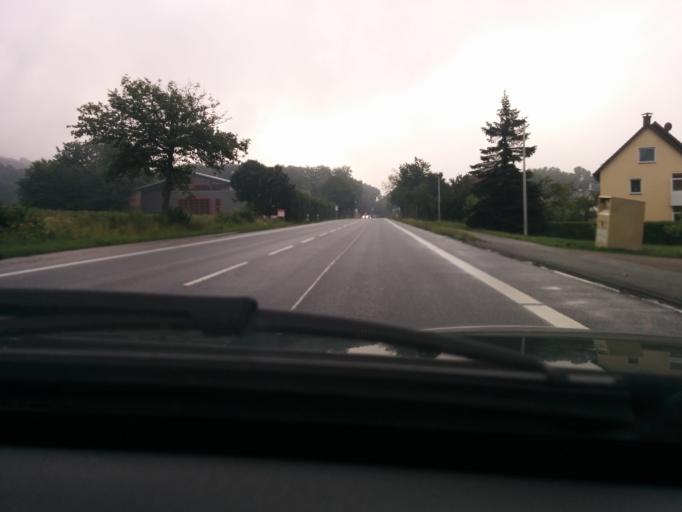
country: DE
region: North Rhine-Westphalia
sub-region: Regierungsbezirk Detmold
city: Steinhagen
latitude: 52.0257
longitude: 8.4160
